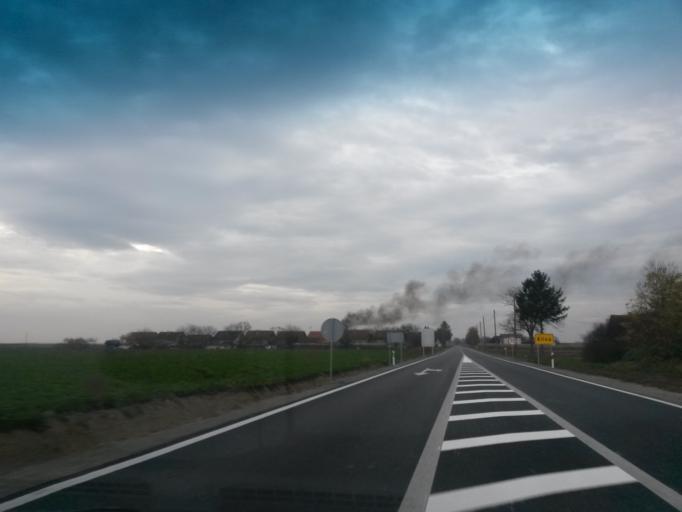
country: HR
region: Osjecko-Baranjska
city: Sarvas
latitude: 45.4824
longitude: 18.8247
